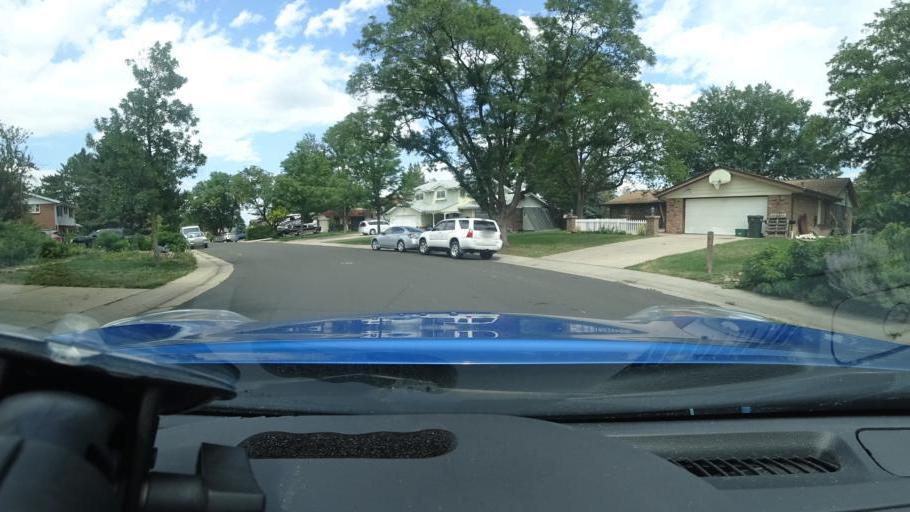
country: US
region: Colorado
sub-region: Adams County
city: Aurora
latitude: 39.7206
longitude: -104.8323
